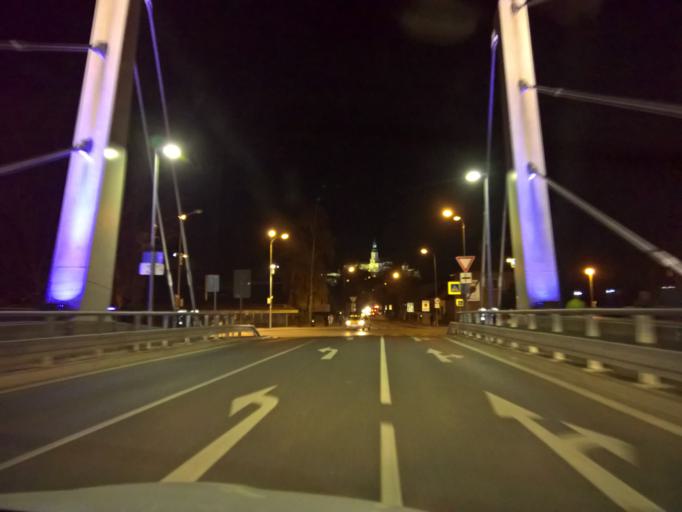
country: SK
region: Nitriansky
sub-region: Okres Nitra
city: Nitra
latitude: 48.3127
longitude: 18.0934
